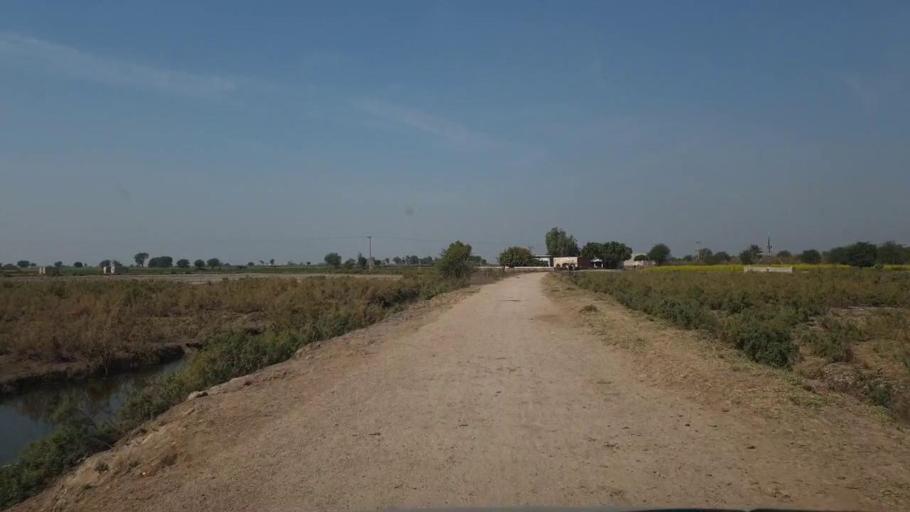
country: PK
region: Sindh
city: Chambar
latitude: 25.3392
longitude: 68.8371
